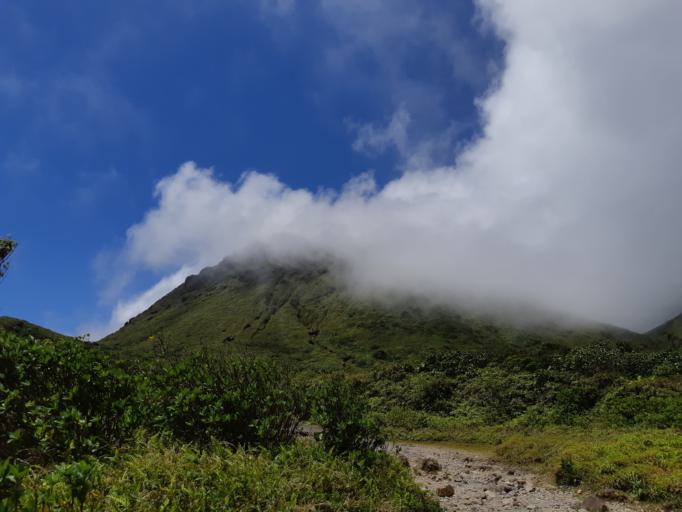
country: GP
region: Guadeloupe
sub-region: Guadeloupe
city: Saint-Claude
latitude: 16.0358
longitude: -61.6656
